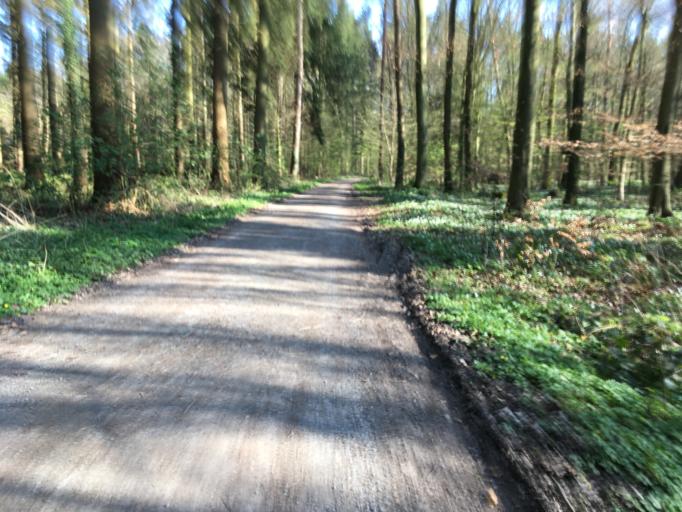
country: DE
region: Baden-Wuerttemberg
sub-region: Regierungsbezirk Stuttgart
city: Leingarten
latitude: 49.1738
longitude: 9.0862
